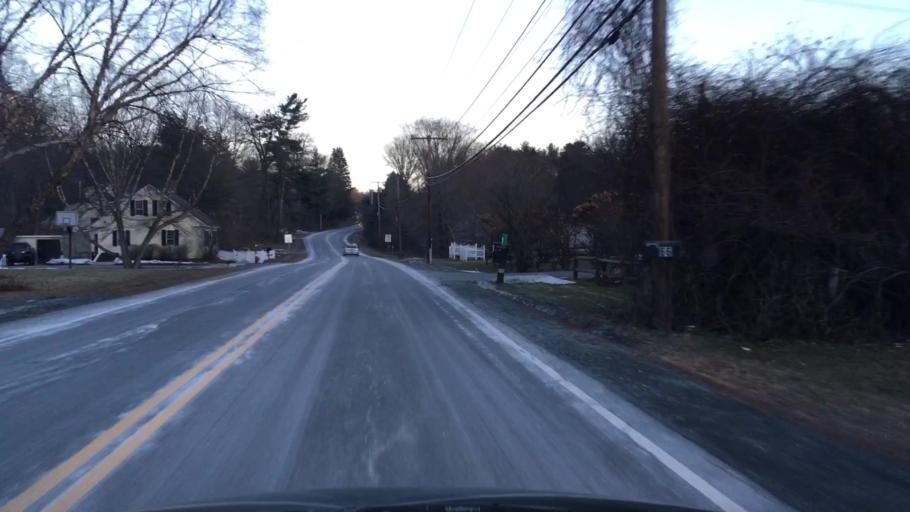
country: US
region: New Hampshire
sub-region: Grafton County
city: Hanover
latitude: 43.6905
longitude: -72.2563
